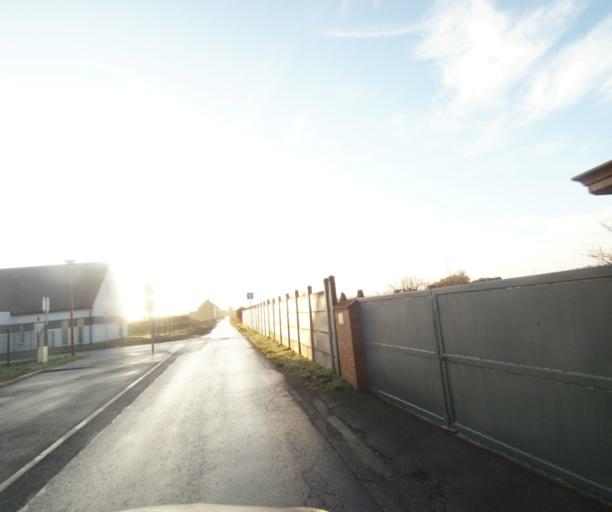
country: FR
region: Nord-Pas-de-Calais
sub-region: Departement du Nord
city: Quarouble
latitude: 50.3898
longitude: 3.6150
